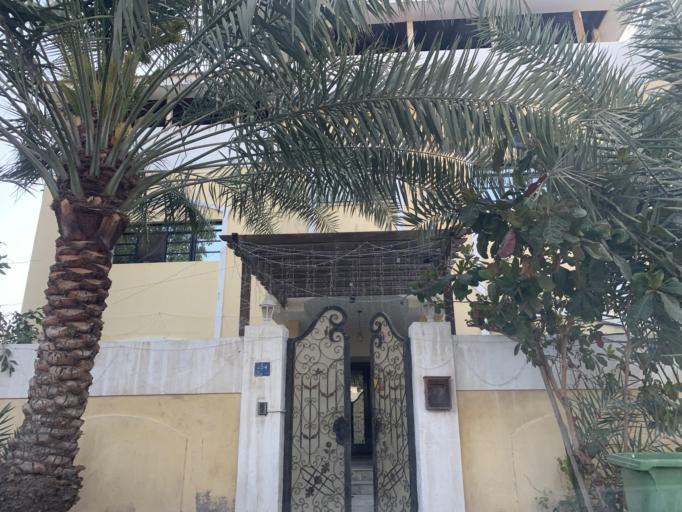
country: BH
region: Manama
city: Manama
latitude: 26.2063
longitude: 50.6031
